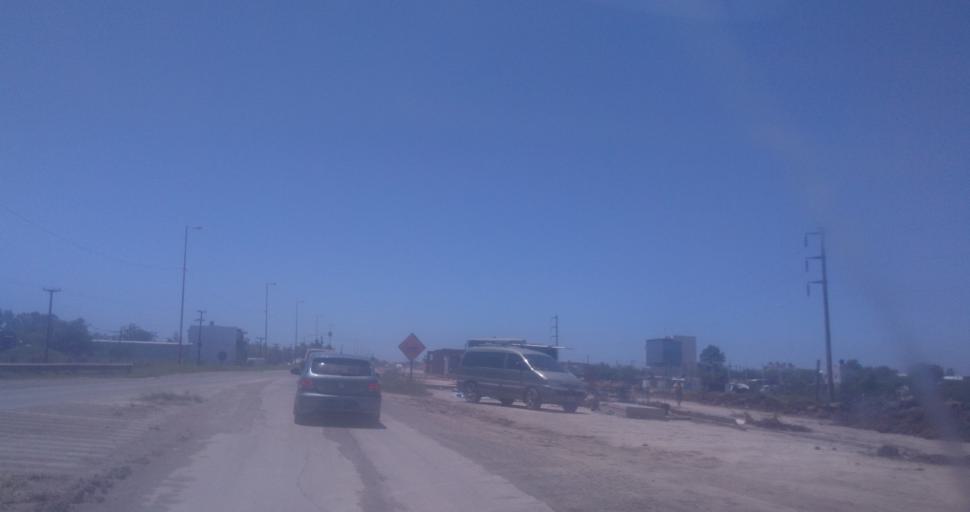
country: AR
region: Chaco
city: Fontana
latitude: -27.4492
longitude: -59.0270
